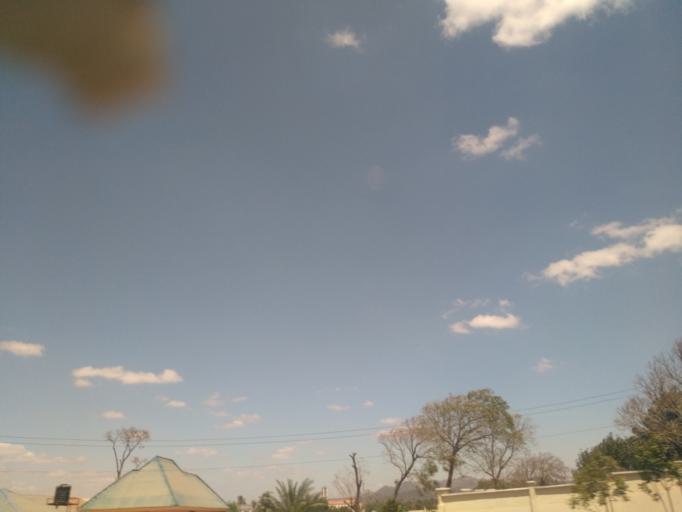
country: TZ
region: Dodoma
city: Dodoma
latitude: -6.1802
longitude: 35.7336
